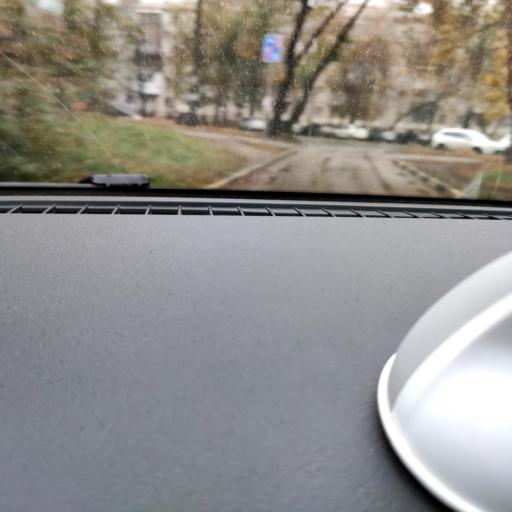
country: RU
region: Samara
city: Samara
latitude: 53.2276
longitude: 50.2079
